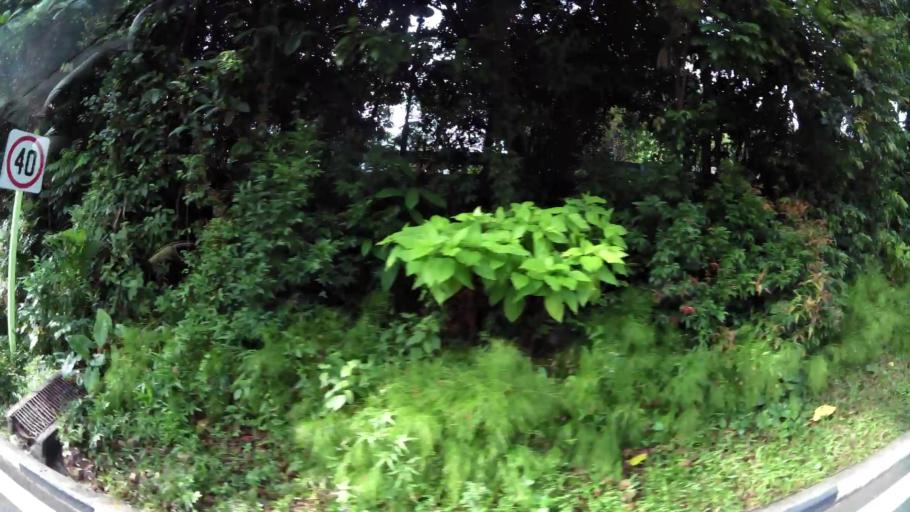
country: SG
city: Singapore
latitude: 1.2549
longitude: 103.8190
